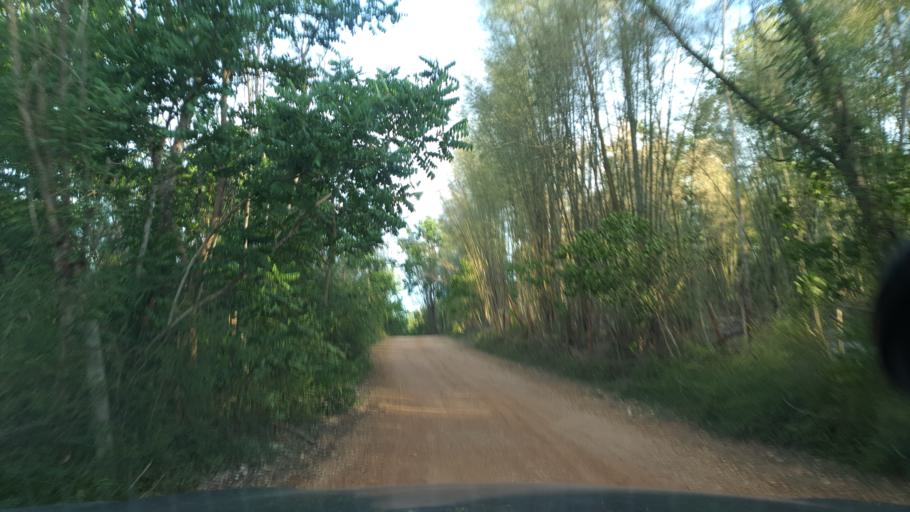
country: TH
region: Lampang
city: Sop Prap
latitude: 17.9559
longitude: 99.3480
